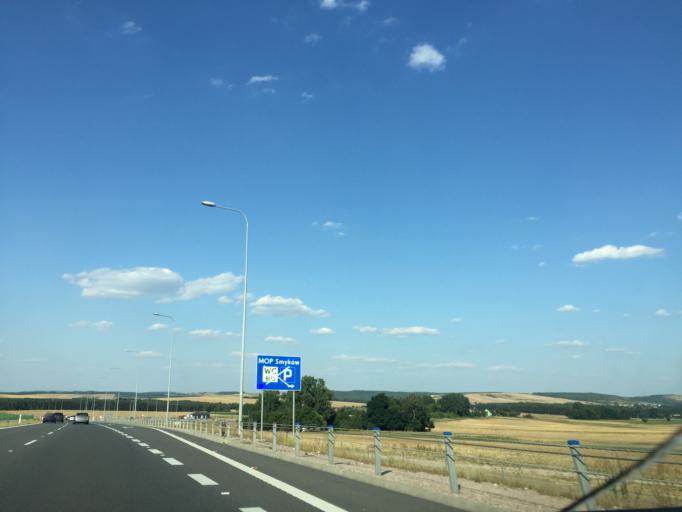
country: PL
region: Swietokrzyskie
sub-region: Powiat jedrzejowski
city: Sobkow
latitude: 50.6990
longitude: 20.3967
